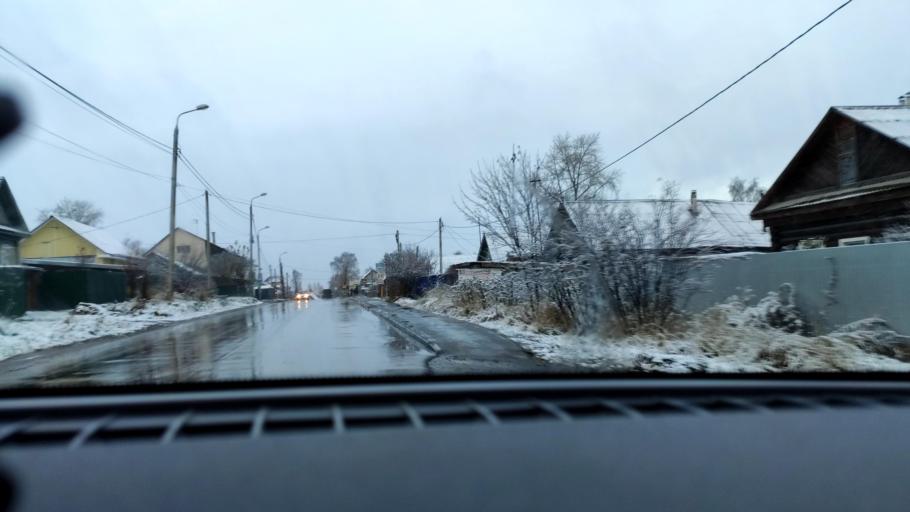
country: RU
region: Perm
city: Kondratovo
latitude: 58.0459
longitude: 56.0536
